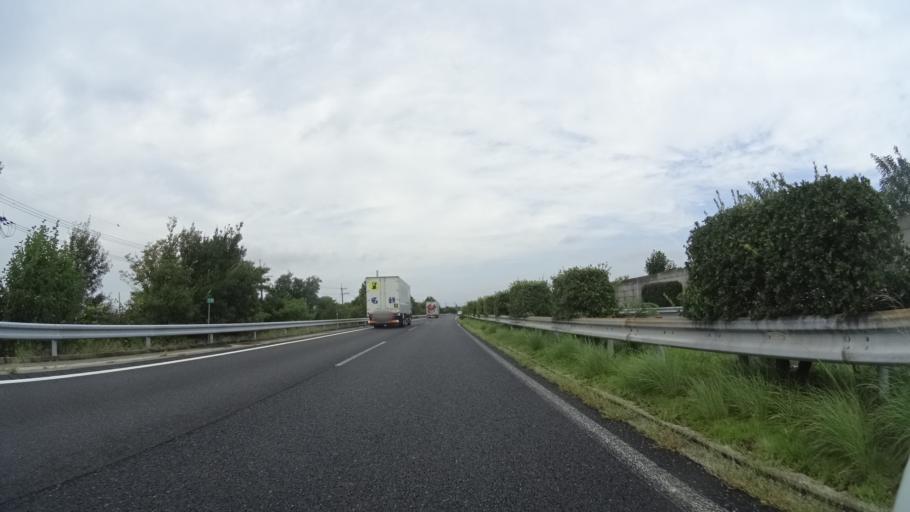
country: JP
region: Hyogo
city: Yashiro
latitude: 34.9288
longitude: 134.9074
